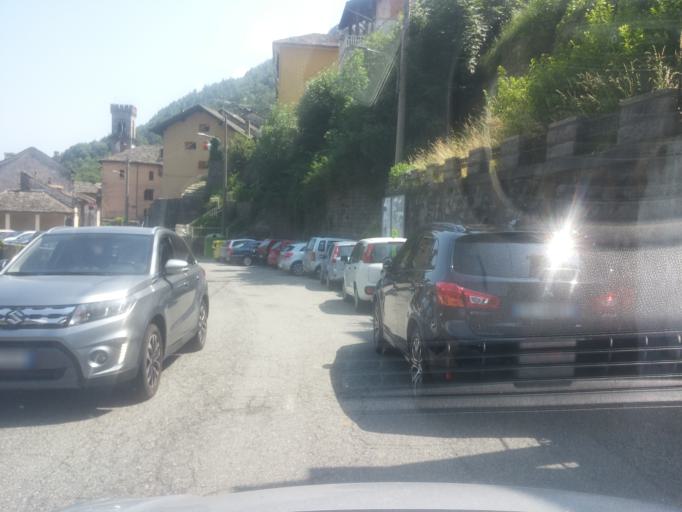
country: IT
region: Piedmont
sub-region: Provincia di Biella
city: Rosazza
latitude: 45.6776
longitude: 7.9763
